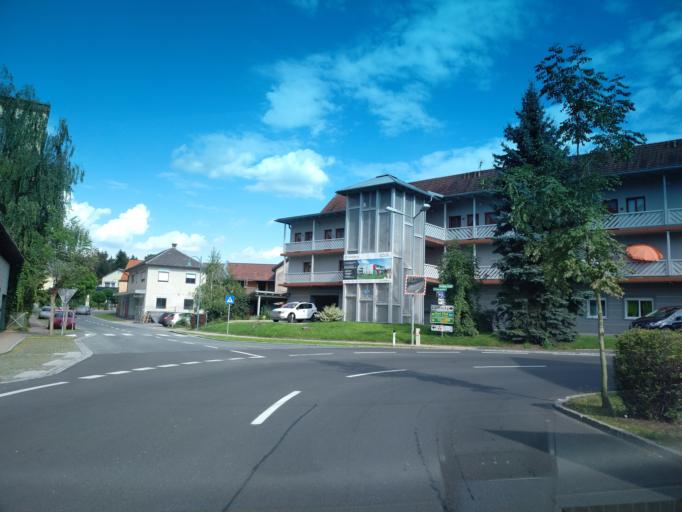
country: AT
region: Styria
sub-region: Politischer Bezirk Leibnitz
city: Kaindorf an der Sulm
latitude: 46.7928
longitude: 15.5330
